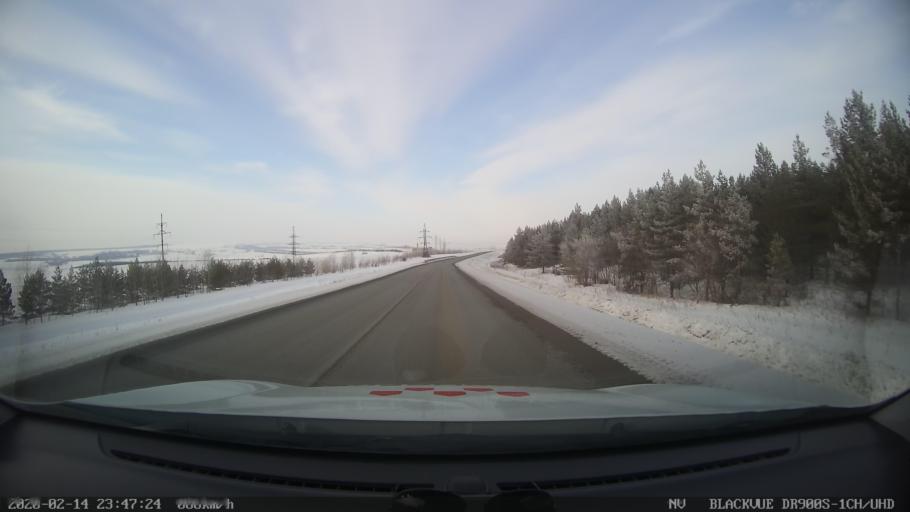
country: RU
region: Tatarstan
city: Kuybyshevskiy Zaton
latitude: 55.2382
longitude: 49.2092
